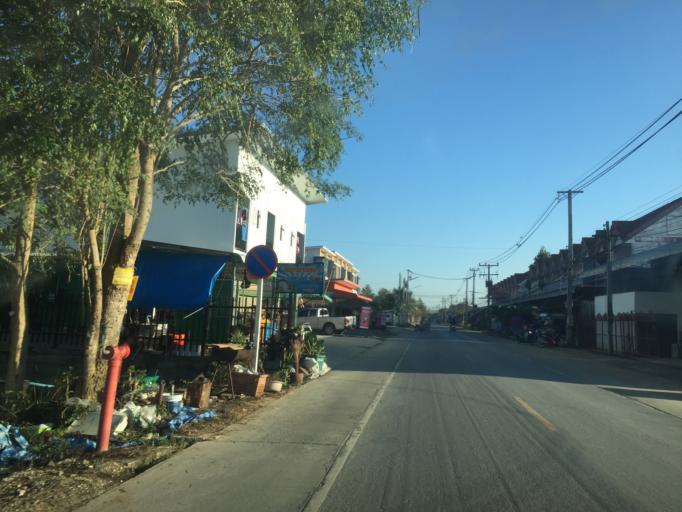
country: TH
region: Lamphun
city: Lamphun
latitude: 18.6039
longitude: 99.0534
